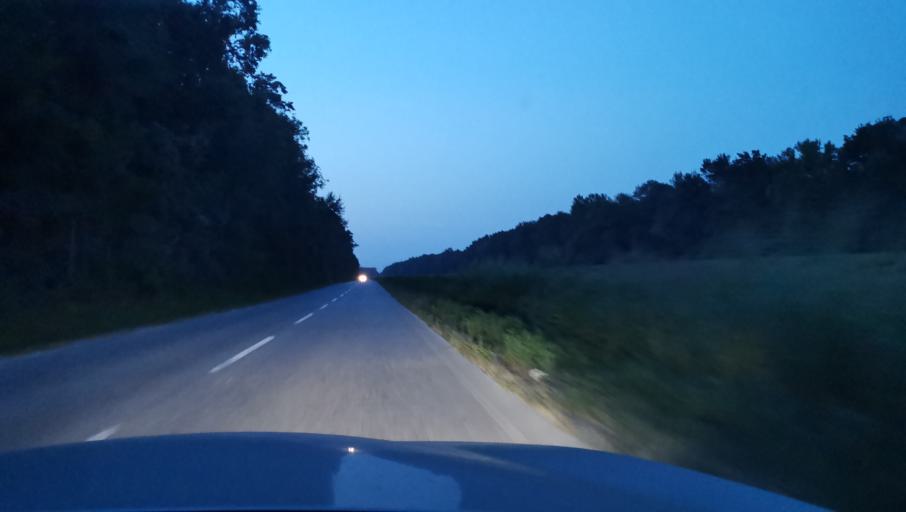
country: RS
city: Boljevci
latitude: 44.6948
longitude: 20.1994
